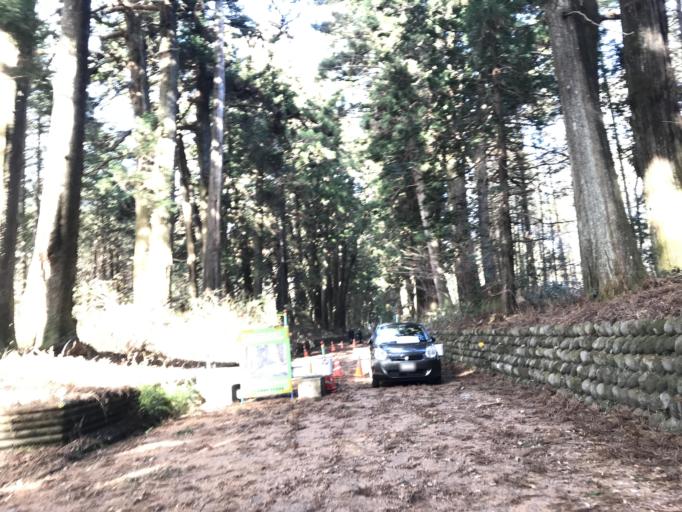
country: JP
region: Tochigi
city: Imaichi
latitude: 36.6764
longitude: 139.7212
